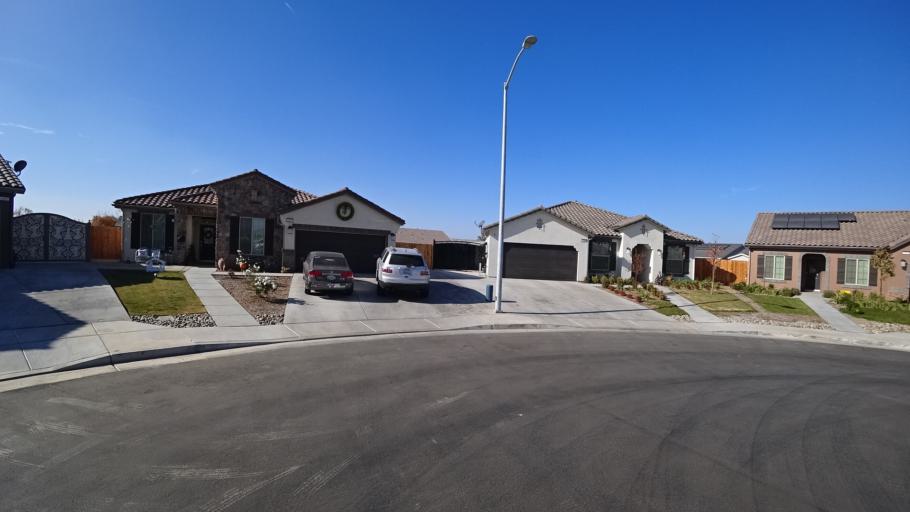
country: US
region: California
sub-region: Kern County
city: Greenfield
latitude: 35.2892
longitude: -119.0691
